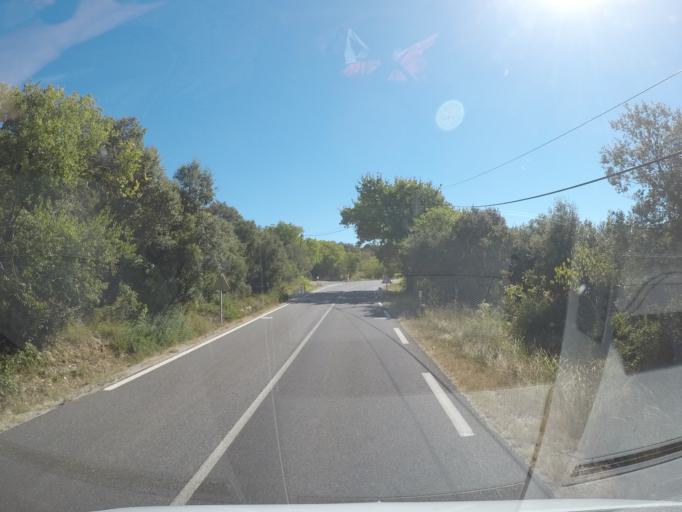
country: FR
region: Languedoc-Roussillon
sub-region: Departement de l'Herault
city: Aniane
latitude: 43.7131
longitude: 3.6134
